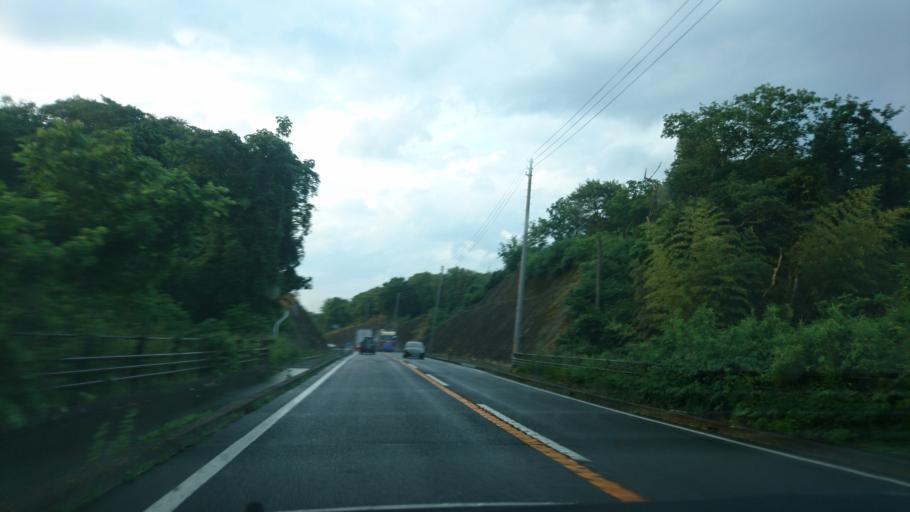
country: JP
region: Iwate
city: Ichinoseki
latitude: 38.9559
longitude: 141.1224
